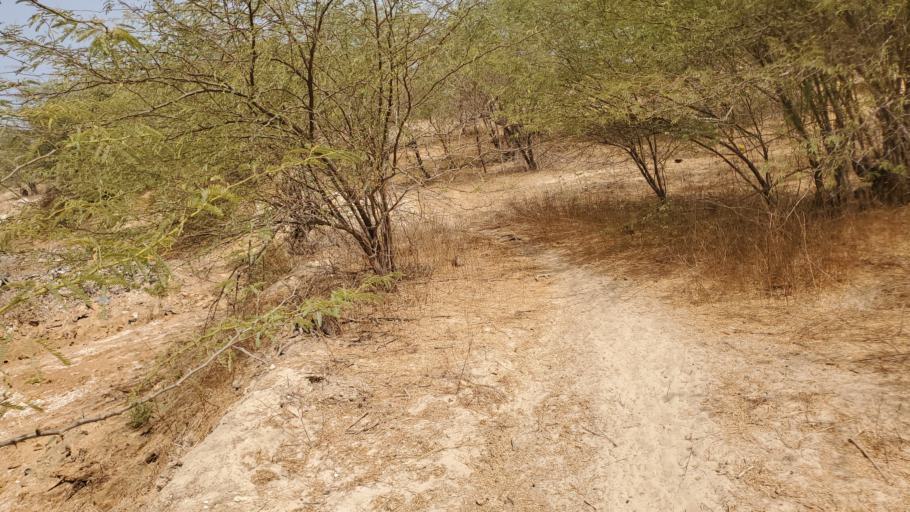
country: SN
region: Saint-Louis
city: Saint-Louis
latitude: 15.9525
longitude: -16.4328
